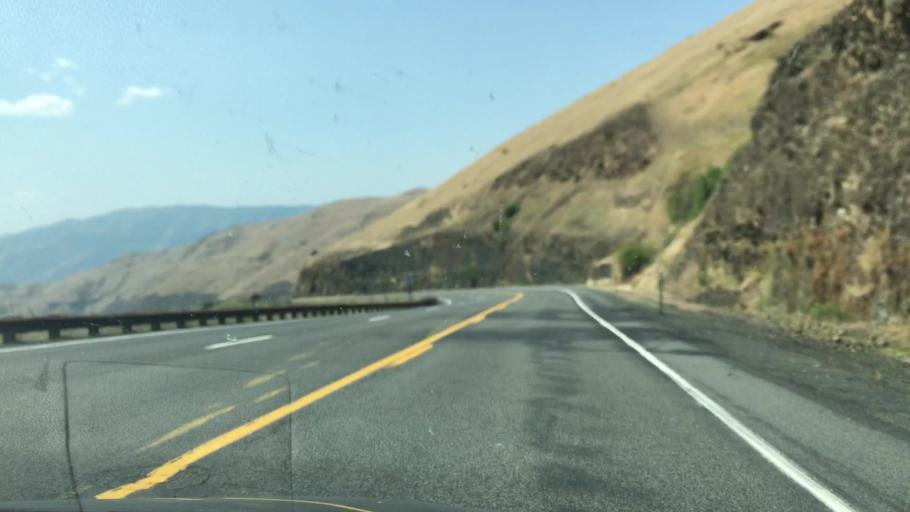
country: US
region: Idaho
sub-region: Idaho County
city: Grangeville
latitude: 45.8261
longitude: -116.2565
